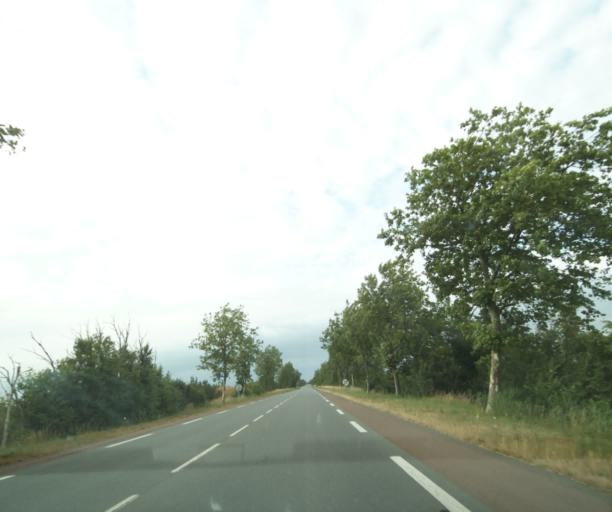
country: FR
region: Poitou-Charentes
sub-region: Departement de la Charente-Maritime
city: Marans
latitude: 46.2869
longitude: -0.9932
